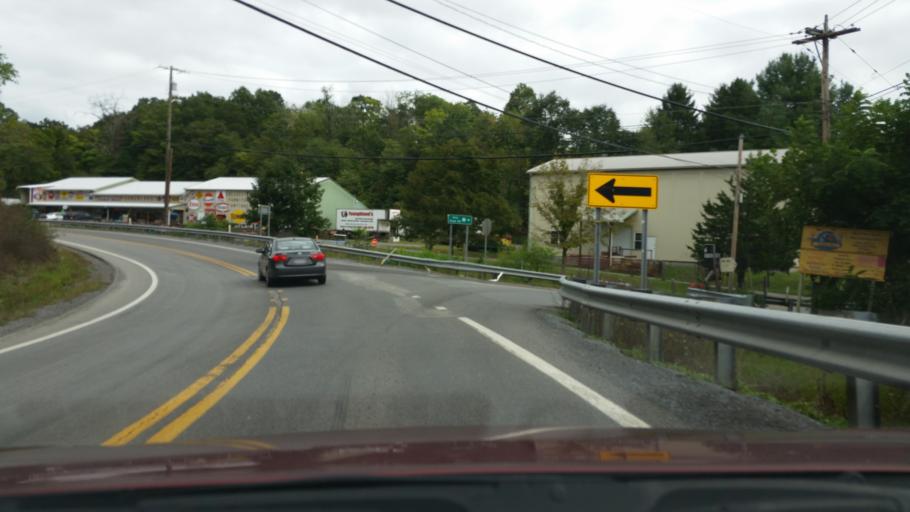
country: US
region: West Virginia
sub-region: Morgan County
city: Berkeley Springs
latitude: 39.6185
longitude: -78.2153
